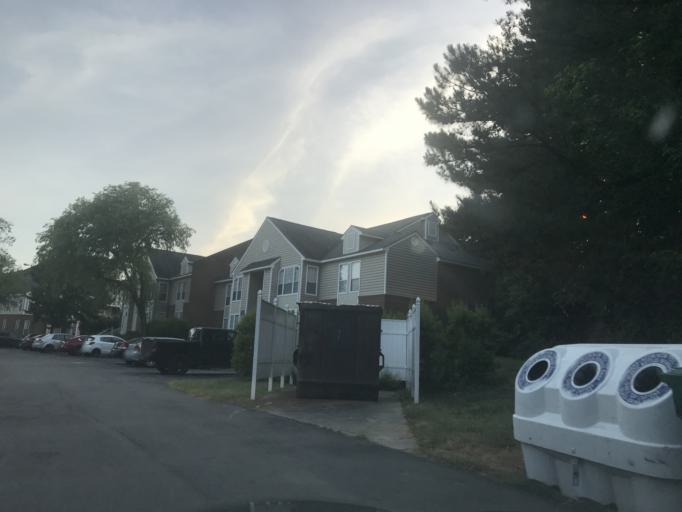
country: US
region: North Carolina
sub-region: Wake County
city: West Raleigh
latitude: 35.8804
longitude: -78.5952
